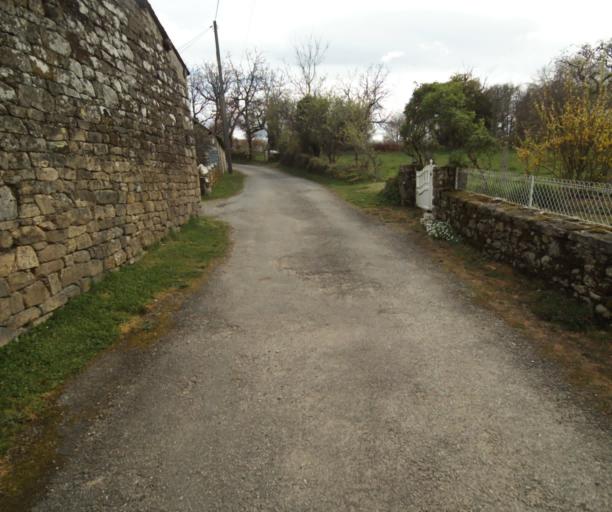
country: FR
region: Limousin
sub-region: Departement de la Correze
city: Argentat
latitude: 45.1828
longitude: 1.9344
